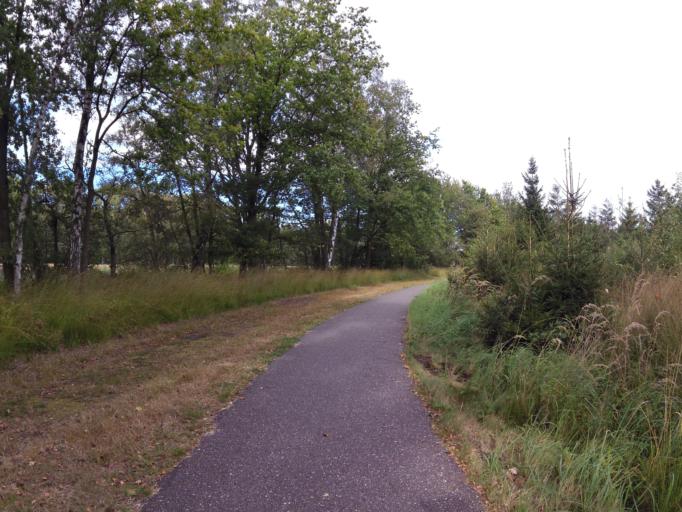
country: NL
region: North Brabant
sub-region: Gemeente Valkenswaard
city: Valkenswaard
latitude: 51.3432
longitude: 5.4932
